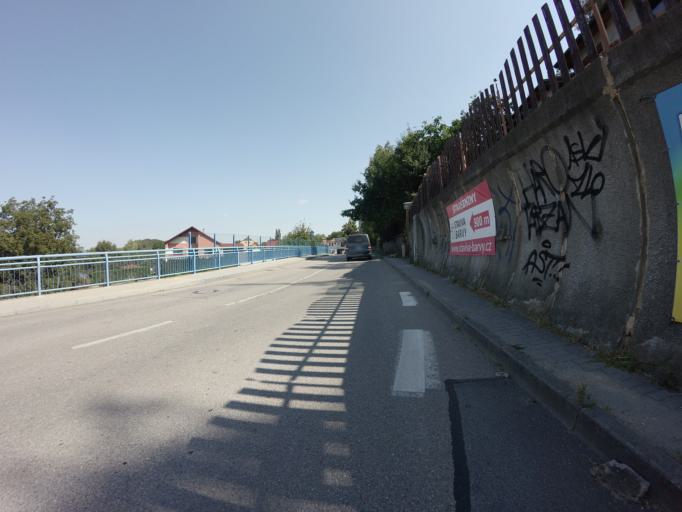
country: CZ
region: Jihocesky
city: Vcelna
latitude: 48.9224
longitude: 14.4372
